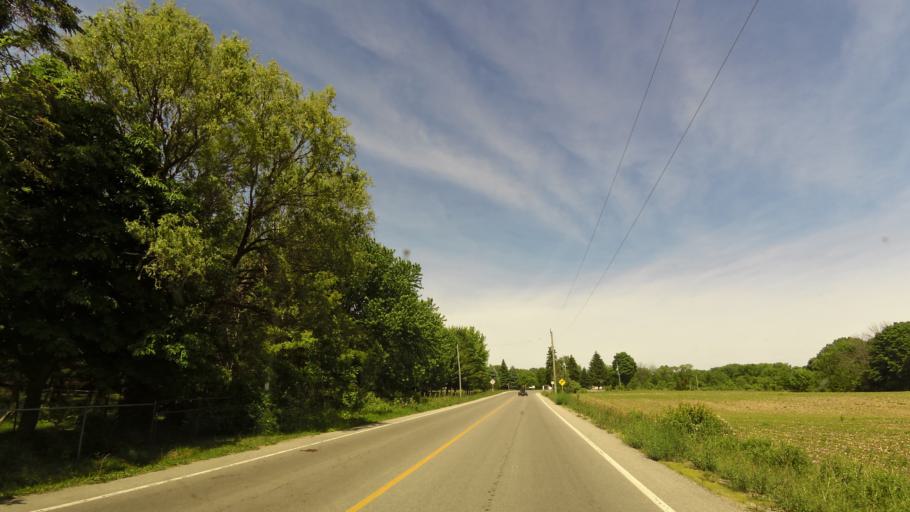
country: CA
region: Ontario
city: Norfolk County
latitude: 42.6642
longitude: -80.4120
